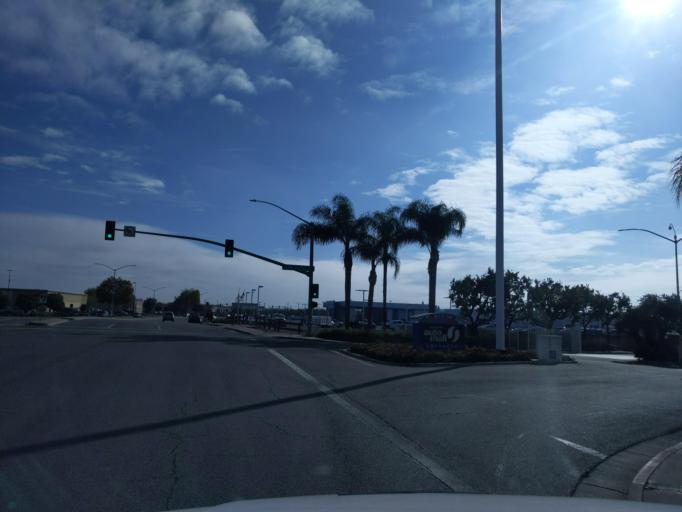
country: US
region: California
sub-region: San Joaquin County
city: Morada
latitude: 38.0202
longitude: -121.2716
